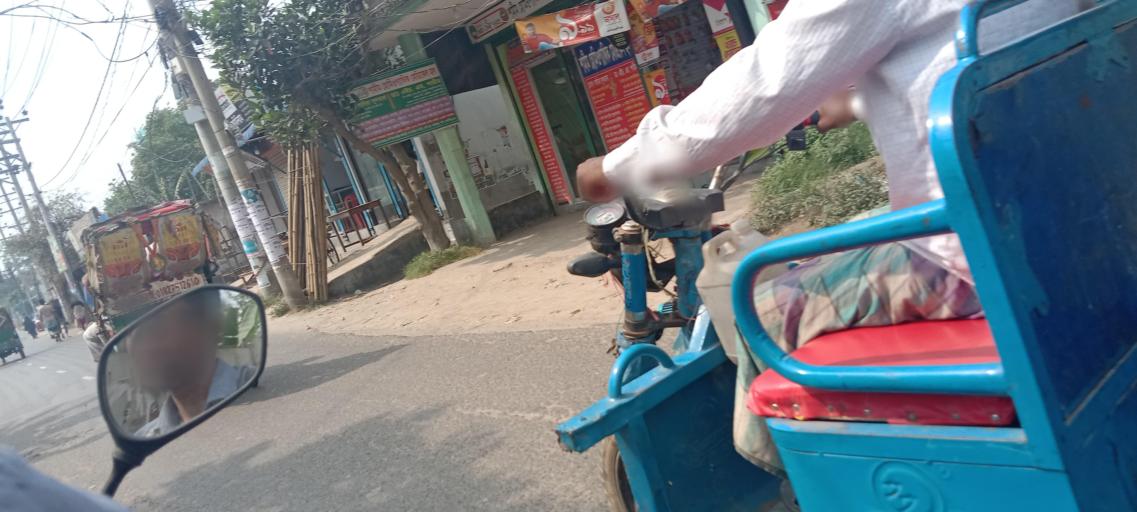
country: BD
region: Dhaka
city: Azimpur
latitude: 23.7148
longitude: 90.3560
